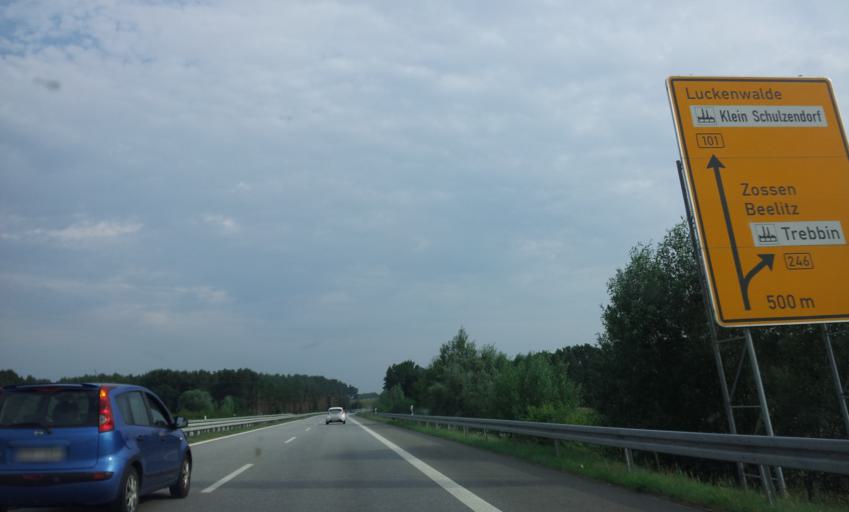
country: DE
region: Brandenburg
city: Trebbin
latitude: 52.2184
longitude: 13.2553
